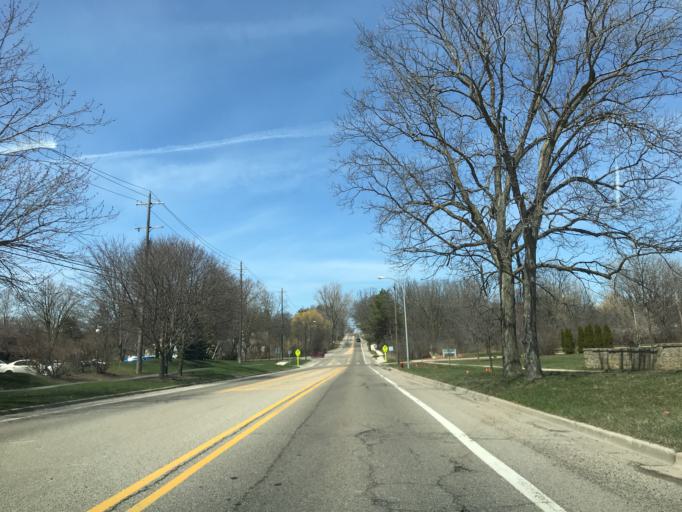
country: US
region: Michigan
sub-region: Washtenaw County
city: Ann Arbor
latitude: 42.3102
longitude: -83.7075
